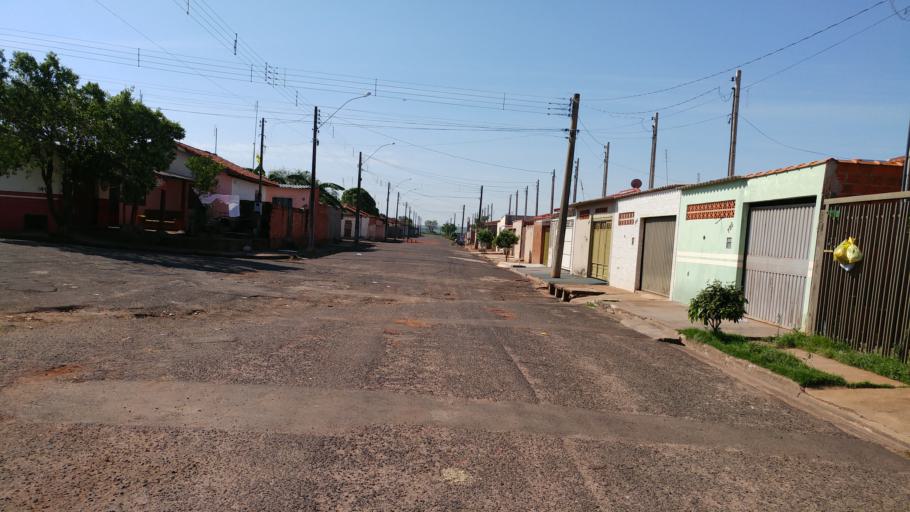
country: BR
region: Sao Paulo
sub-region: Paraguacu Paulista
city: Paraguacu Paulista
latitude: -22.4093
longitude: -50.5632
